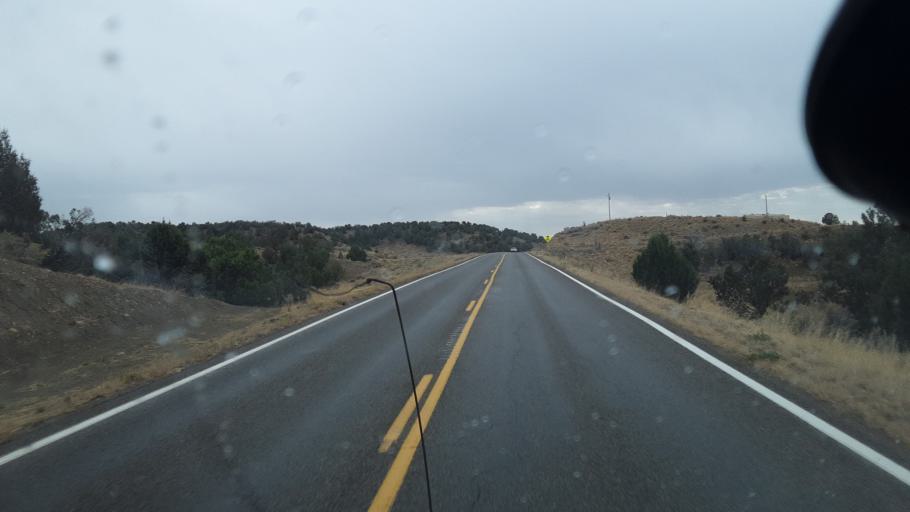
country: US
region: New Mexico
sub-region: San Juan County
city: Spencerville
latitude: 37.0248
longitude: -108.1822
